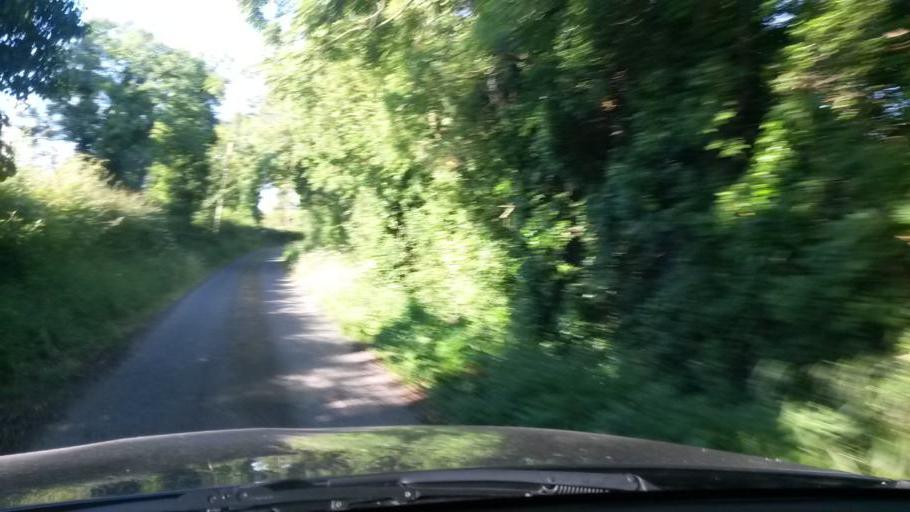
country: IE
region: Leinster
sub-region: Dublin City
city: Finglas
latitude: 53.4356
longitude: -6.3252
